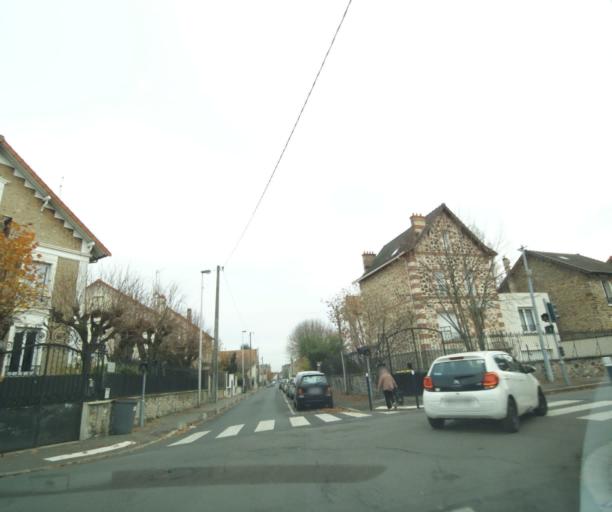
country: FR
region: Ile-de-France
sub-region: Departement de Seine-Saint-Denis
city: Villemomble
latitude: 48.8848
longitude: 2.5146
